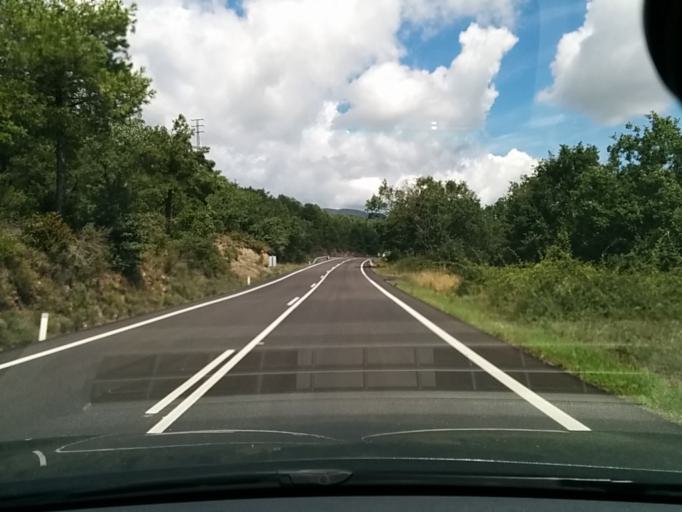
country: ES
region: Aragon
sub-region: Provincia de Huesca
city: Labuerda
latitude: 42.4399
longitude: 0.1304
